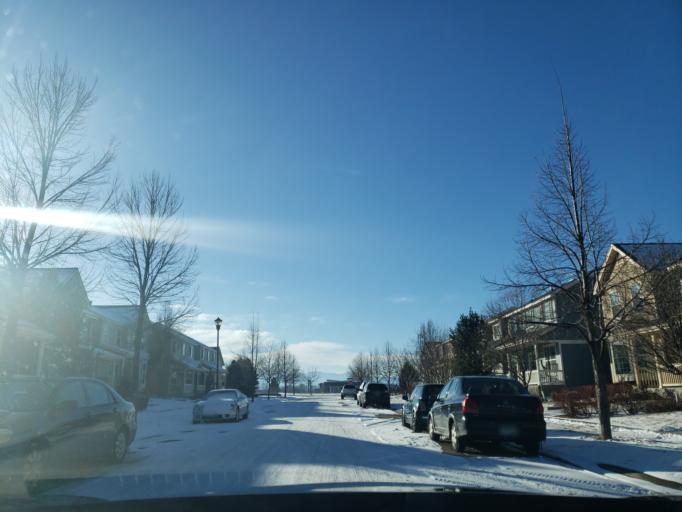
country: US
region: Colorado
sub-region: Larimer County
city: Fort Collins
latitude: 40.5136
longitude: -105.0089
